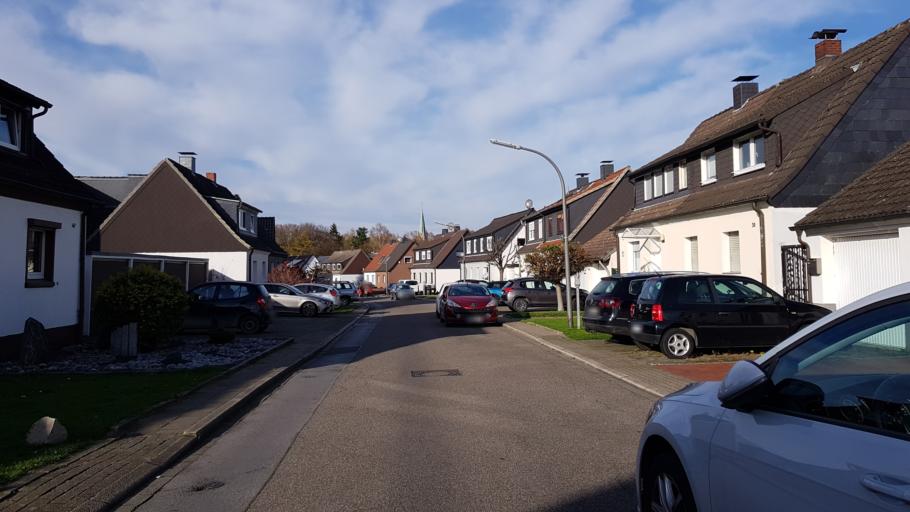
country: DE
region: North Rhine-Westphalia
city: Bochum-Hordel
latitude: 51.4906
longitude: 7.1552
